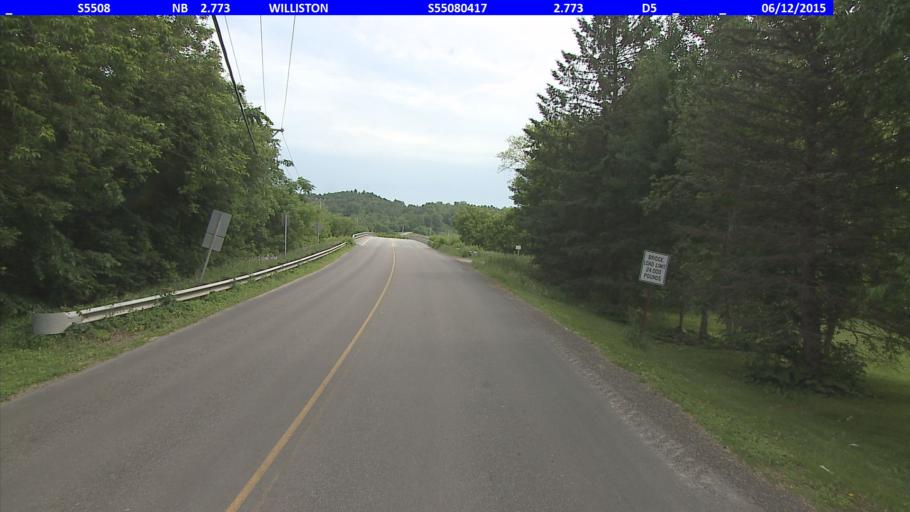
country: US
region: Vermont
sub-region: Chittenden County
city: Williston
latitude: 44.4700
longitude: -73.0442
